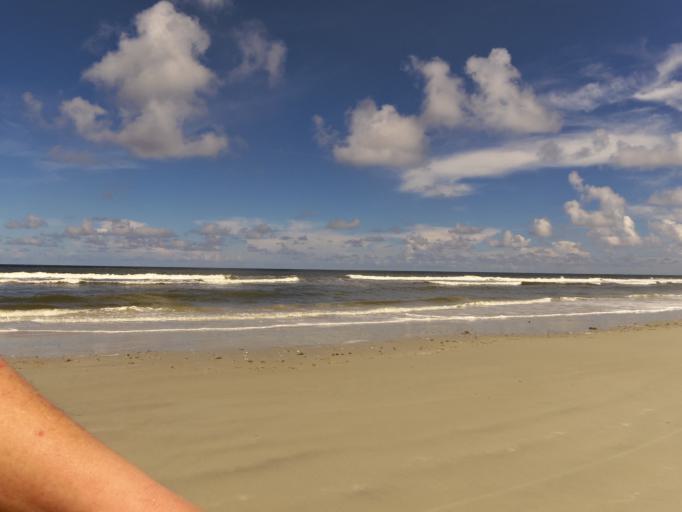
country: US
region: Florida
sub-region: Duval County
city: Atlantic Beach
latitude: 30.4777
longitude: -81.4134
